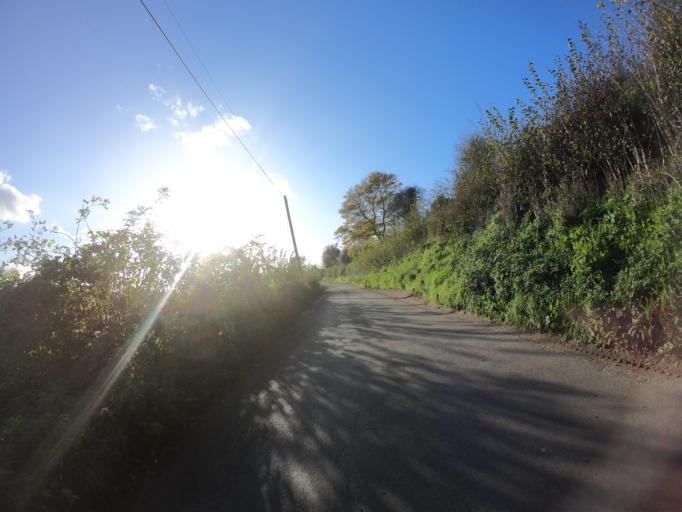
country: GB
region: England
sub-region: Kent
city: Eynsford
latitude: 51.3679
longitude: 0.2002
